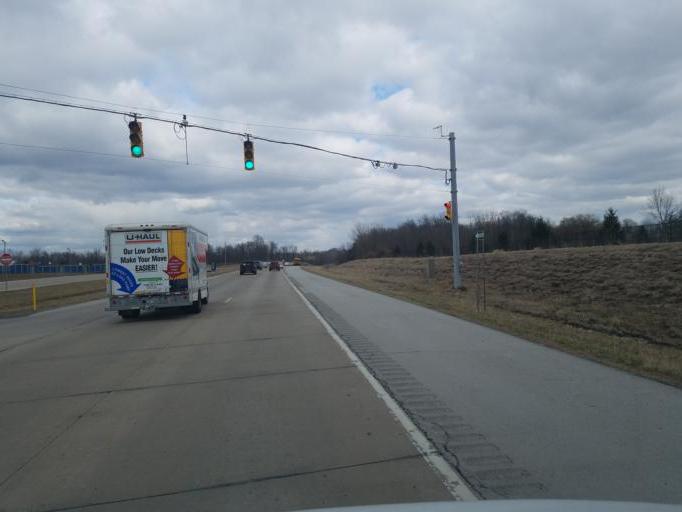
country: US
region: Indiana
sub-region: Hendricks County
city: Avon
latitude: 39.7611
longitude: -86.4270
